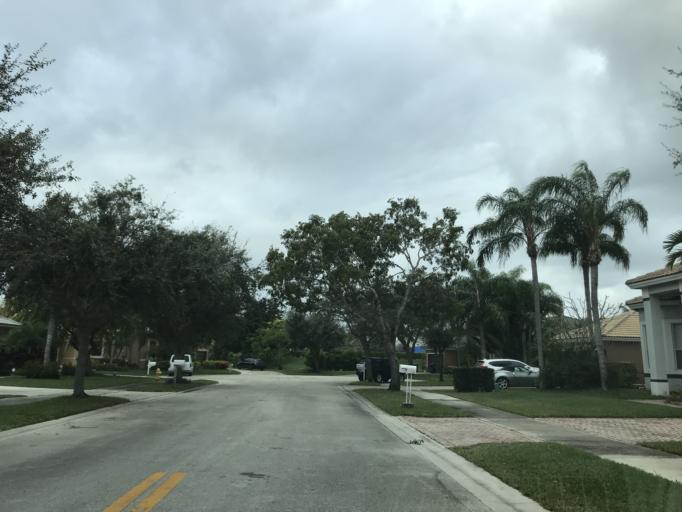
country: US
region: Florida
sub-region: Broward County
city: Coral Springs
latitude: 26.2986
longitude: -80.2753
